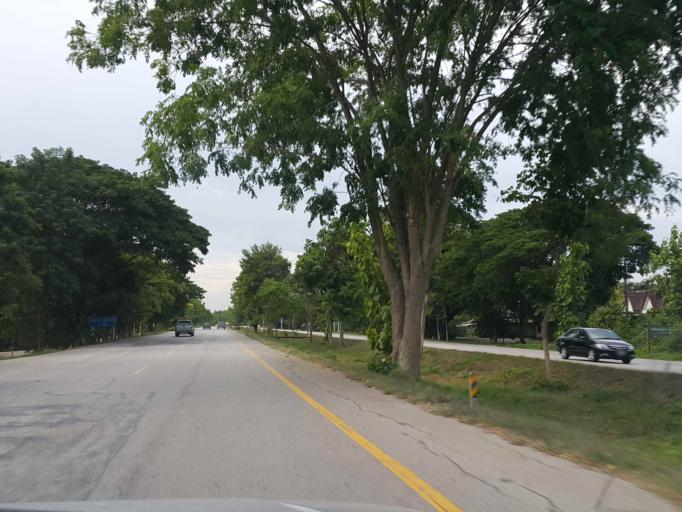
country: TH
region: Lampang
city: Ko Kha
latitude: 18.1745
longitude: 99.4076
